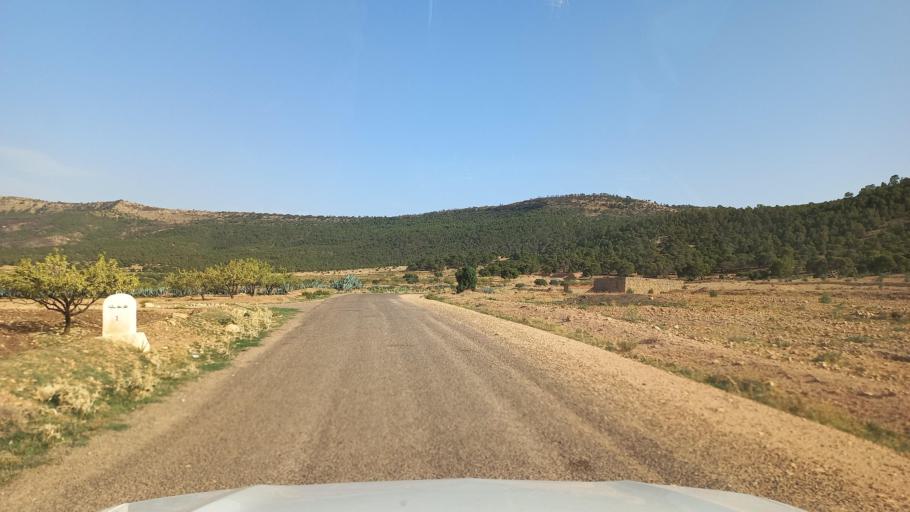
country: TN
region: Al Qasrayn
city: Kasserine
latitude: 35.3366
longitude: 8.8381
